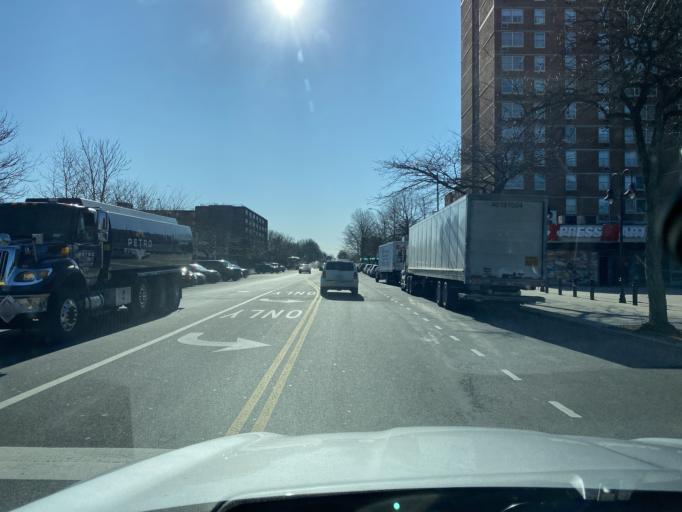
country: US
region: New York
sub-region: Bronx
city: The Bronx
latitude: 40.8219
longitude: -73.8583
